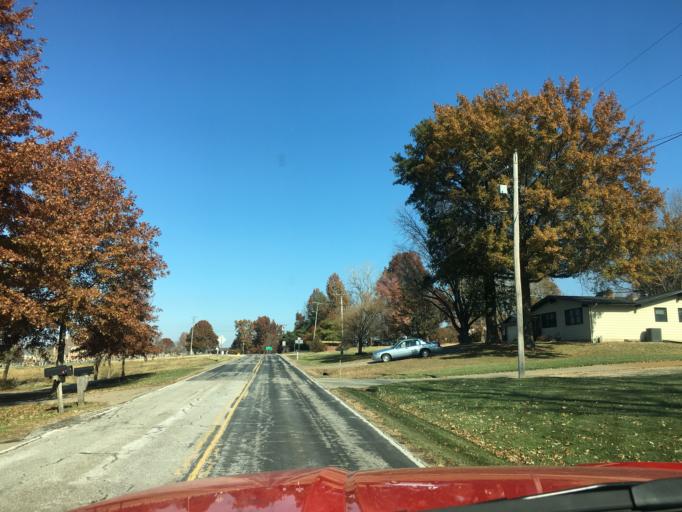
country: US
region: Missouri
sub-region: Cole County
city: Wardsville
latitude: 38.4849
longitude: -92.1760
